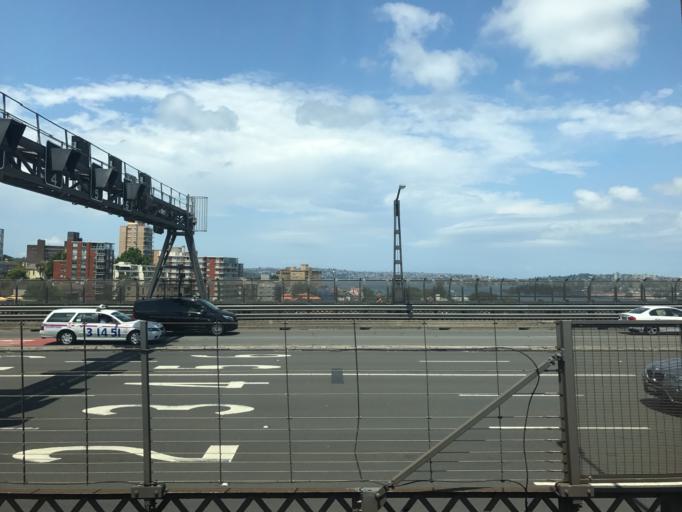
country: AU
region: New South Wales
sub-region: North Sydney
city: Milsons Point
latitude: -33.8493
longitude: 151.2124
